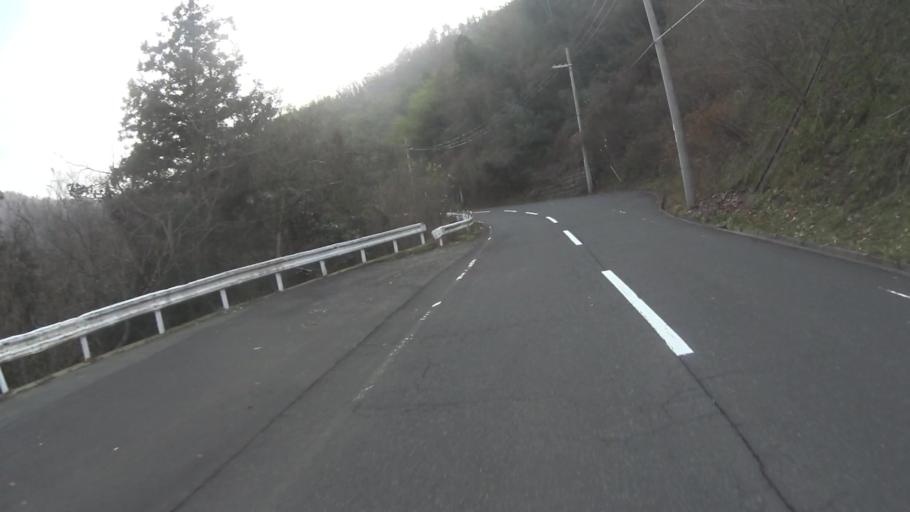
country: JP
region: Kyoto
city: Maizuru
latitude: 35.4387
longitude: 135.3995
